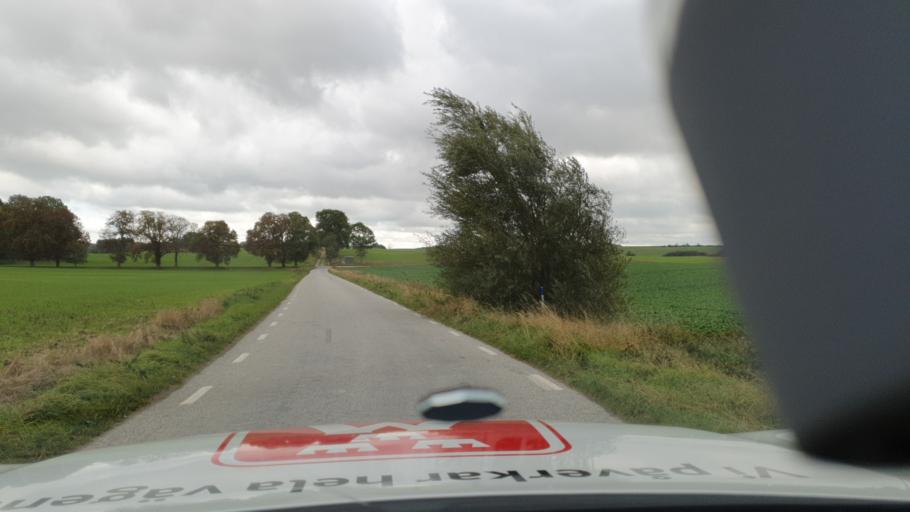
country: SE
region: Skane
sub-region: Svedala Kommun
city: Svedala
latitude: 55.4879
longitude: 13.1870
